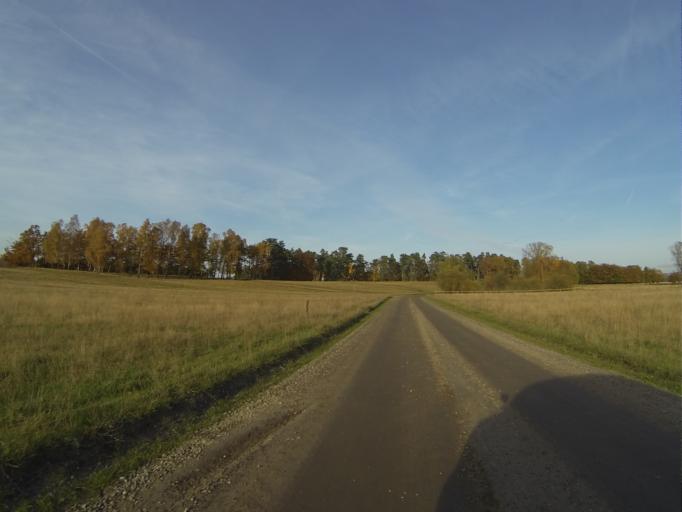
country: SE
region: Skane
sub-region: Lunds Kommun
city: Veberod
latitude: 55.7143
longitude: 13.4349
